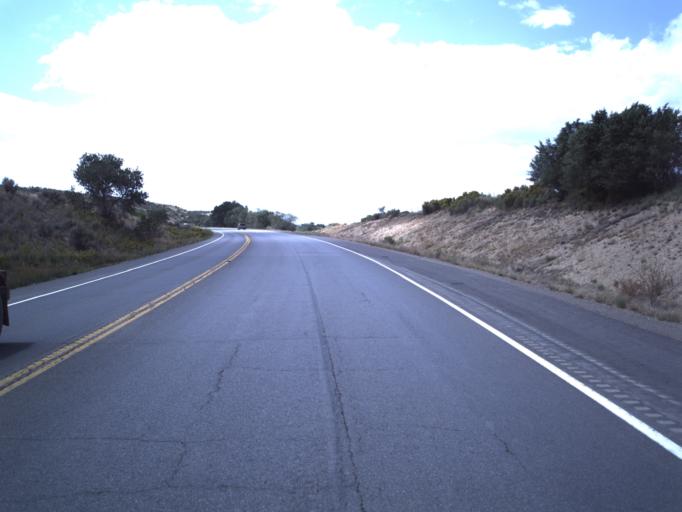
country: US
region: Utah
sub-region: Duchesne County
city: Duchesne
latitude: 40.1695
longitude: -110.3043
